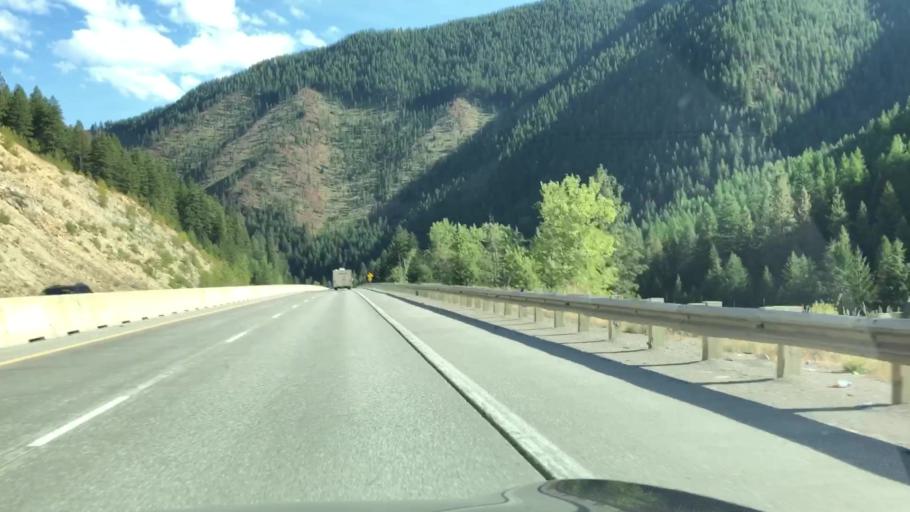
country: US
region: Montana
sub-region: Sanders County
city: Thompson Falls
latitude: 47.3066
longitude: -115.2058
